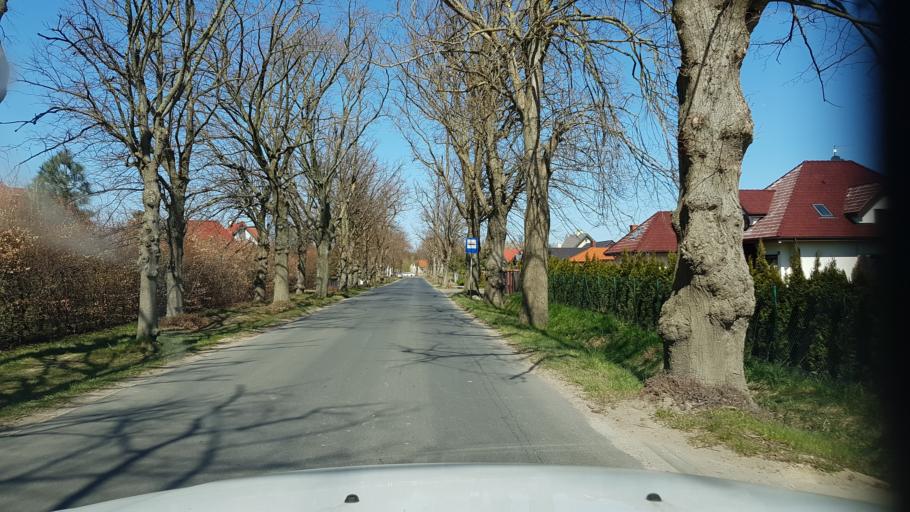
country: PL
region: West Pomeranian Voivodeship
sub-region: Koszalin
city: Koszalin
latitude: 54.2389
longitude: 16.1631
